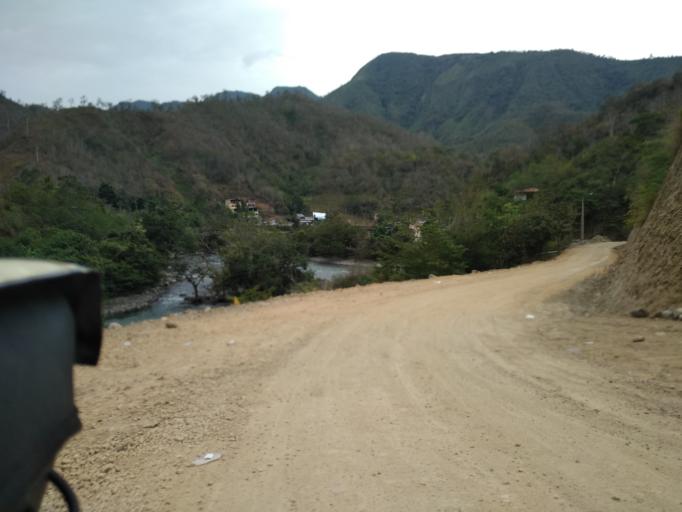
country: PE
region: Cajamarca
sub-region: Provincia de San Ignacio
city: Namballe
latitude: -4.9757
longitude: -79.1137
